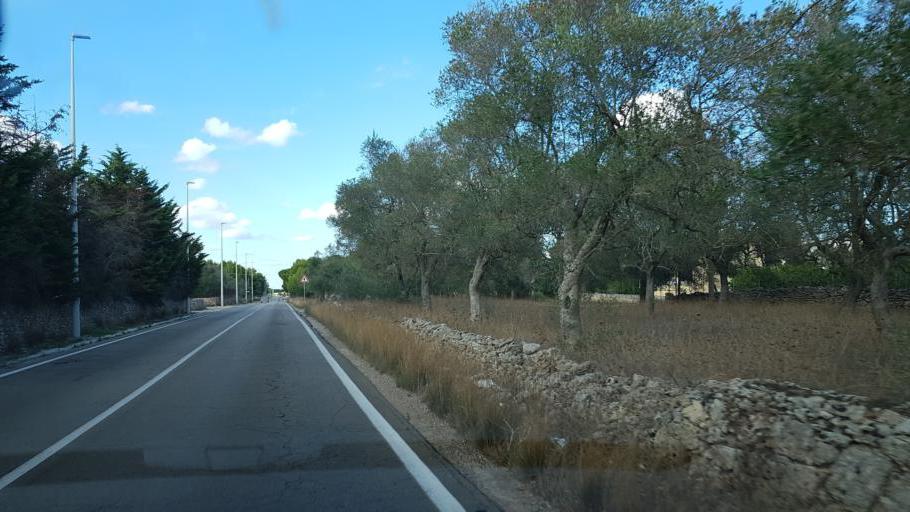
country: IT
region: Apulia
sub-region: Provincia di Lecce
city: Nardo
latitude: 40.1411
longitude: 18.0189
